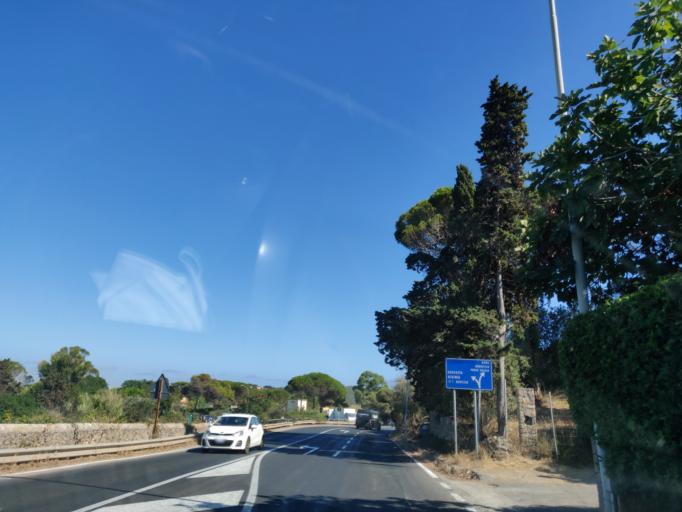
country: IT
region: Tuscany
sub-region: Provincia di Grosseto
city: Monte Argentario
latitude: 42.4339
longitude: 11.1568
